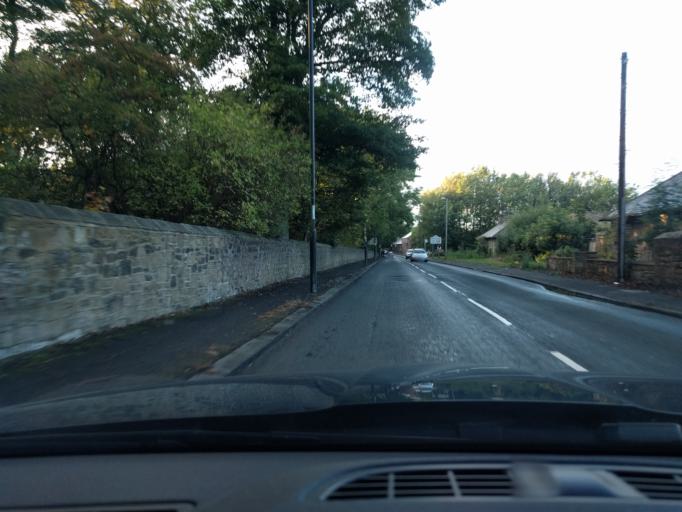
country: GB
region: England
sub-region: Northumberland
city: Backworth
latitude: 55.0393
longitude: -1.5270
